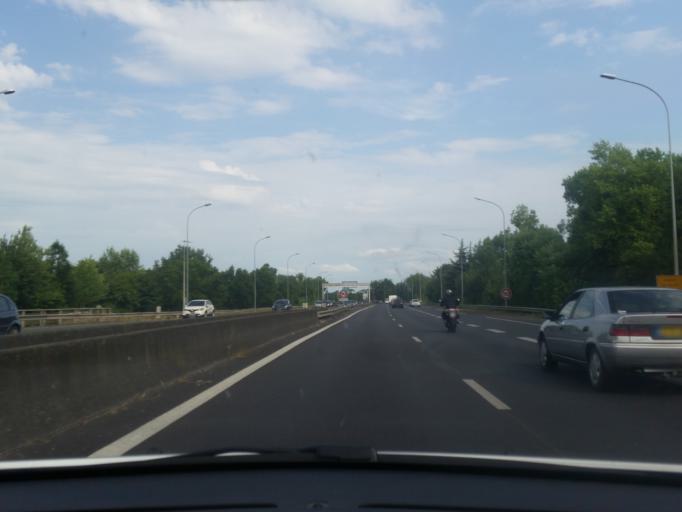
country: FR
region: Pays de la Loire
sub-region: Departement de Maine-et-Loire
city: Avrille
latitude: 47.4679
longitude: -0.5853
